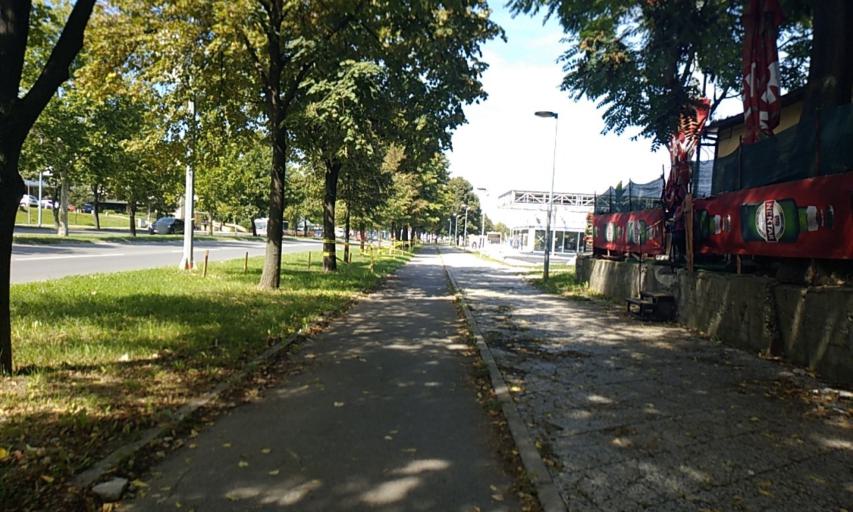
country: BA
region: Republika Srpska
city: Banja Luka
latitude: 44.7853
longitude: 17.2060
